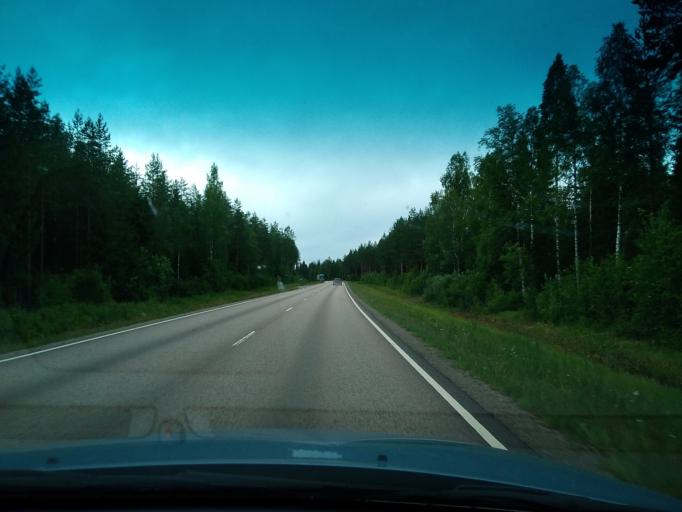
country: FI
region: Central Finland
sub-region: Keuruu
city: Multia
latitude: 62.3802
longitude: 24.7490
